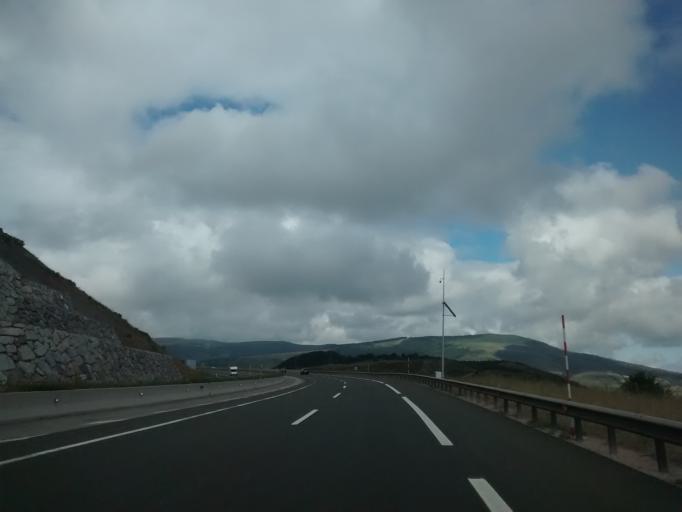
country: ES
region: Cantabria
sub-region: Provincia de Cantabria
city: Reinosa
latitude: 43.0218
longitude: -4.1188
